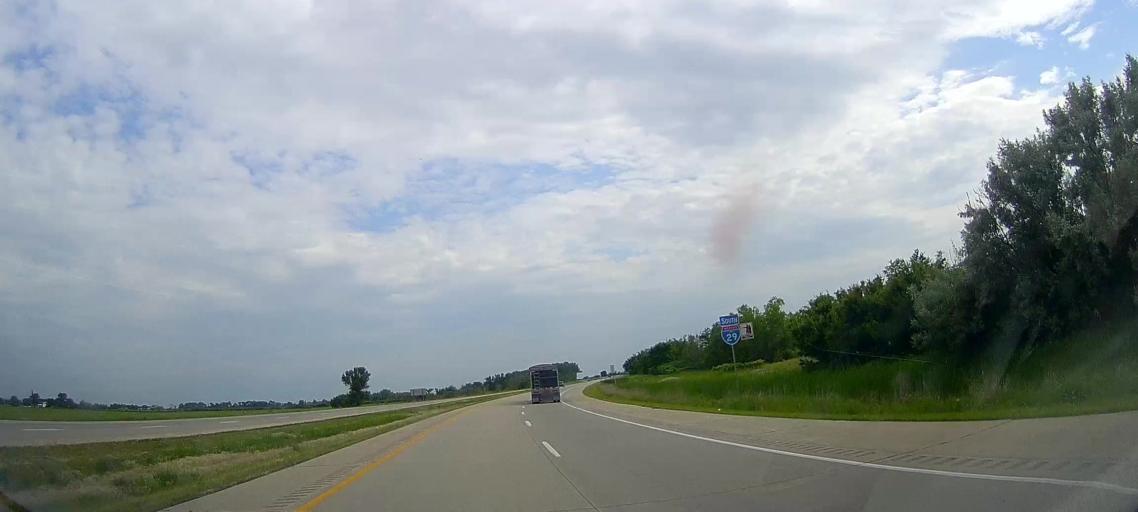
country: US
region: Nebraska
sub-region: Burt County
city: Tekamah
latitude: 41.7951
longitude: -96.0510
